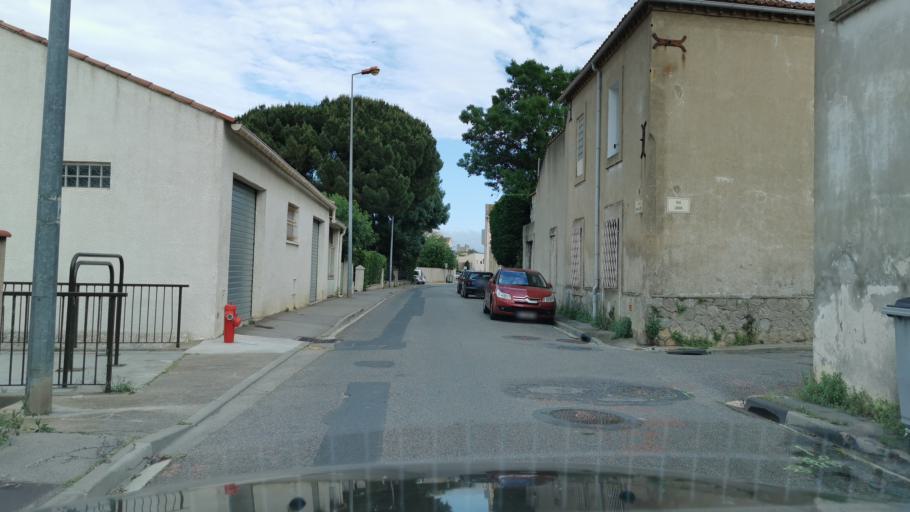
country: FR
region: Languedoc-Roussillon
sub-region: Departement de l'Aude
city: Narbonne
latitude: 43.1876
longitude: 2.9927
